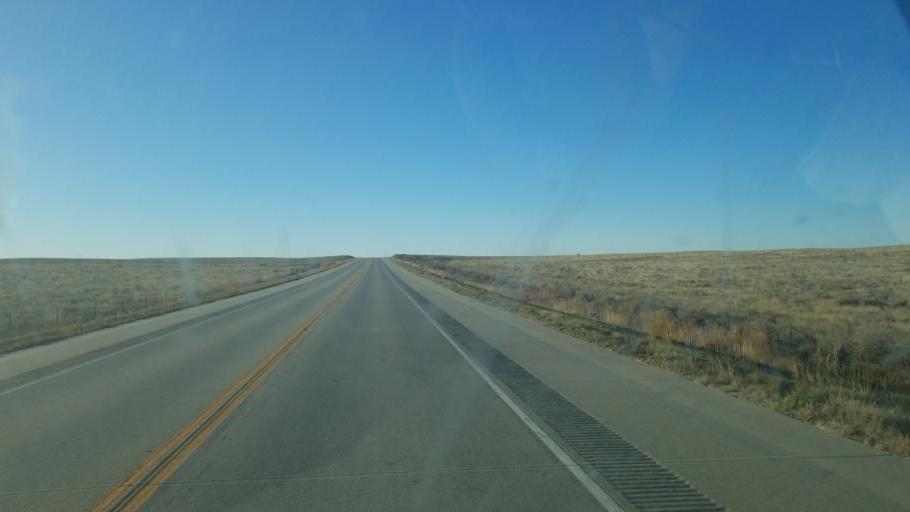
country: US
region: Colorado
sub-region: Kiowa County
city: Eads
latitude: 38.5438
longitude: -102.7860
